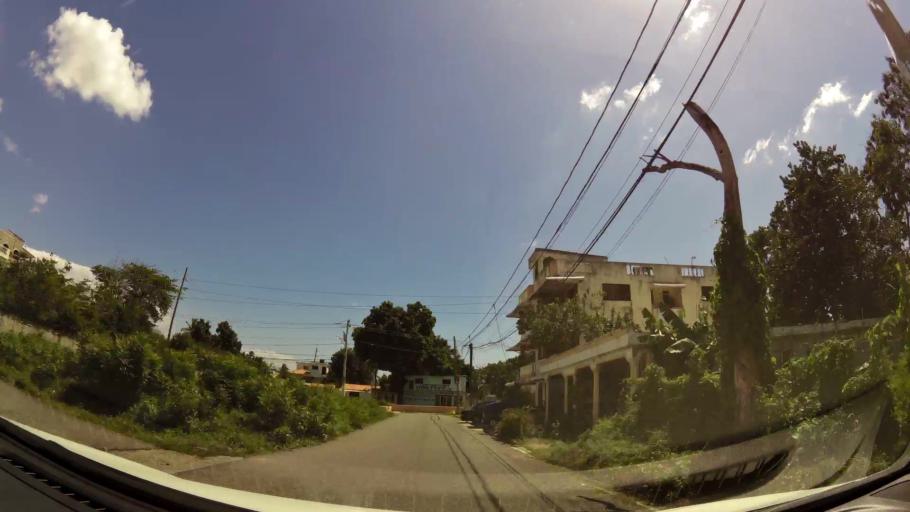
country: DO
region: San Cristobal
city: San Cristobal
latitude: 18.4162
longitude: -70.0916
